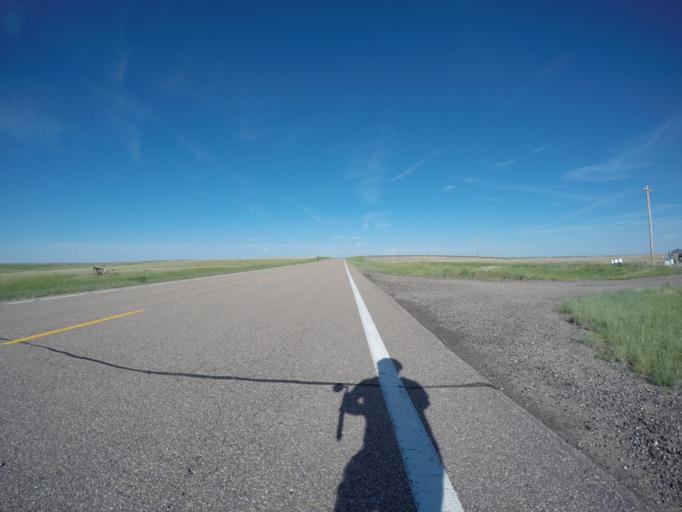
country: US
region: Kansas
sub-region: Cheyenne County
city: Saint Francis
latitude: 39.7566
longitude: -101.9542
